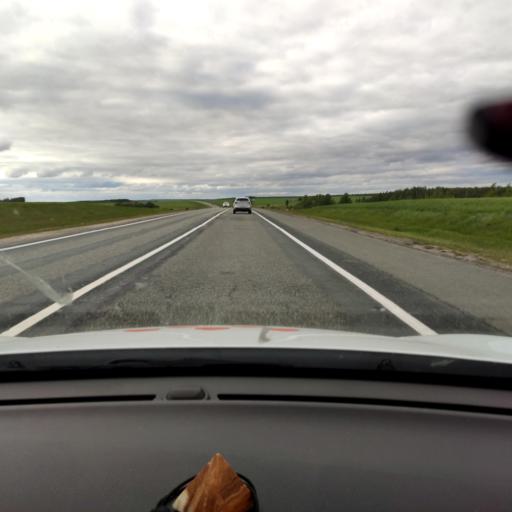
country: RU
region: Tatarstan
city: Rybnaya Sloboda
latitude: 55.4813
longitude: 49.8467
